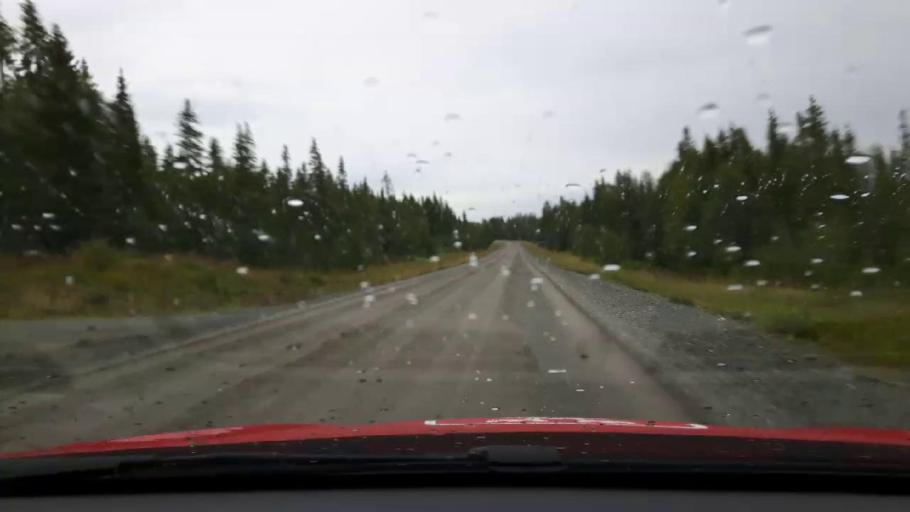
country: SE
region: Jaemtland
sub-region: Are Kommun
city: Are
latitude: 63.4663
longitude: 12.6161
